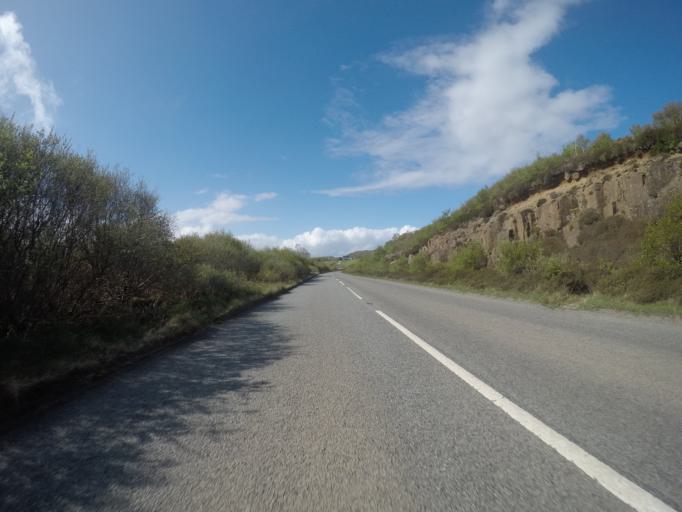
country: GB
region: Scotland
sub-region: Highland
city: Portree
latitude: 57.6070
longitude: -6.1726
